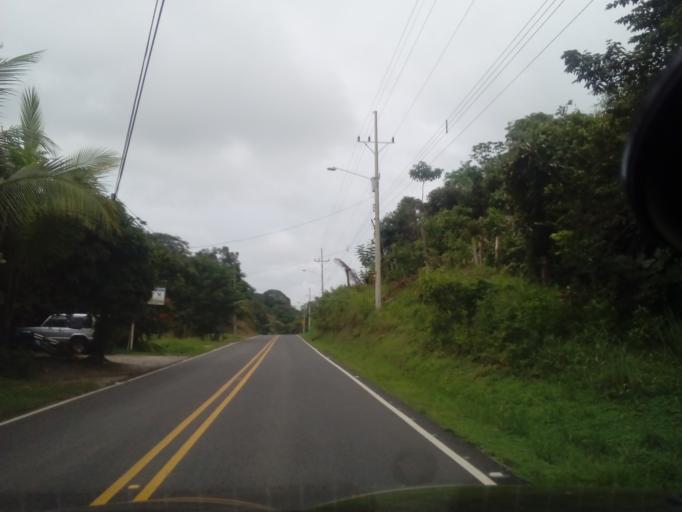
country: CR
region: Guanacaste
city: Samara
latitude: 9.9303
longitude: -85.5164
